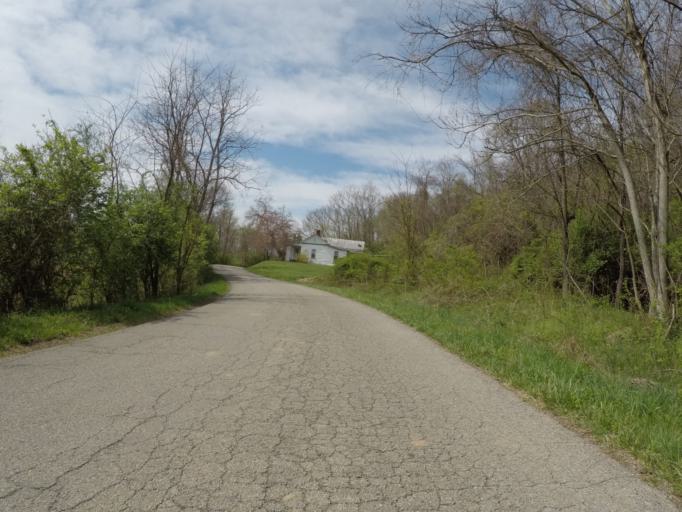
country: US
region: West Virginia
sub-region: Wayne County
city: Lavalette
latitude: 38.3443
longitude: -82.3800
